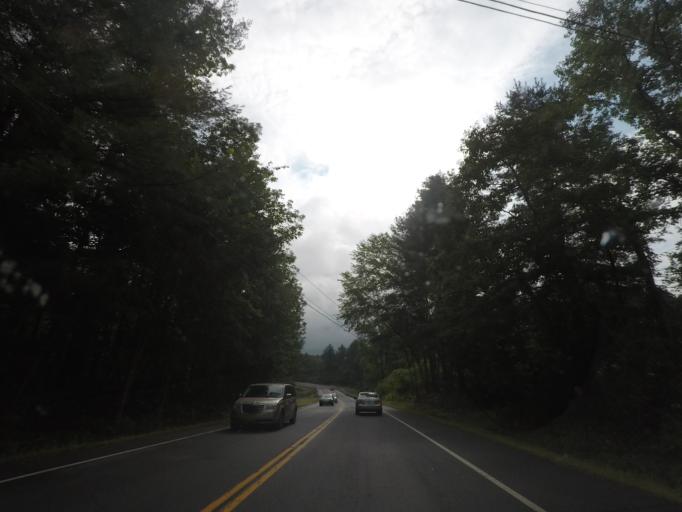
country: US
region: New York
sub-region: Rensselaer County
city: Nassau
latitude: 42.4952
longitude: -73.5374
